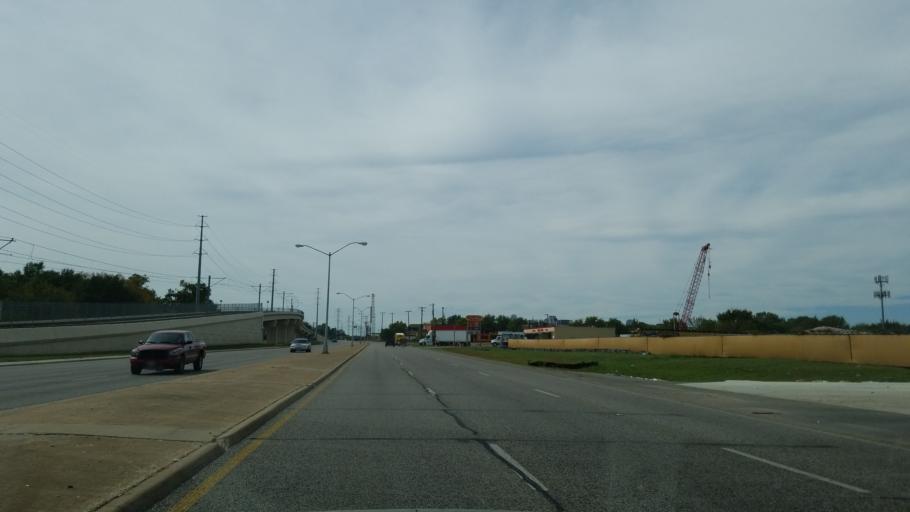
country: US
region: Texas
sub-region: Dallas County
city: Dallas
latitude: 32.7665
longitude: -96.7335
